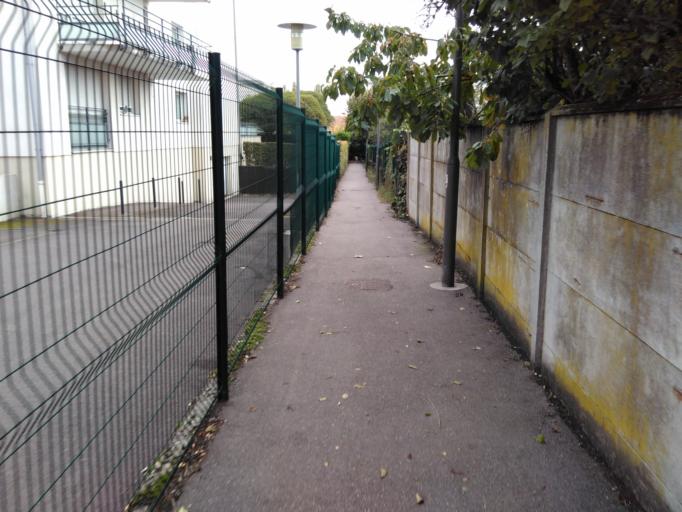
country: FR
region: Lorraine
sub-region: Departement de Meurthe-et-Moselle
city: Essey-les-Nancy
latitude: 48.7049
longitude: 6.2253
